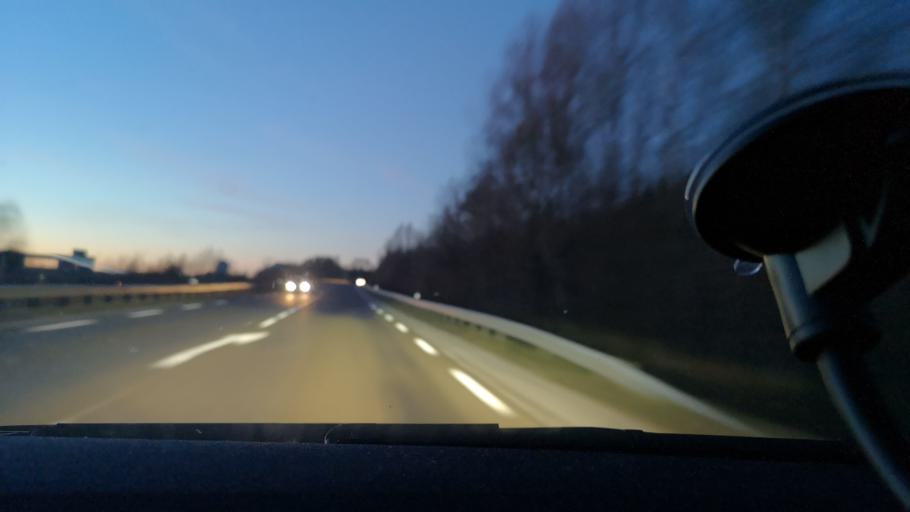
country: FR
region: Franche-Comte
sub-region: Departement du Jura
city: Champagnole
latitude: 46.7508
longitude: 5.9189
